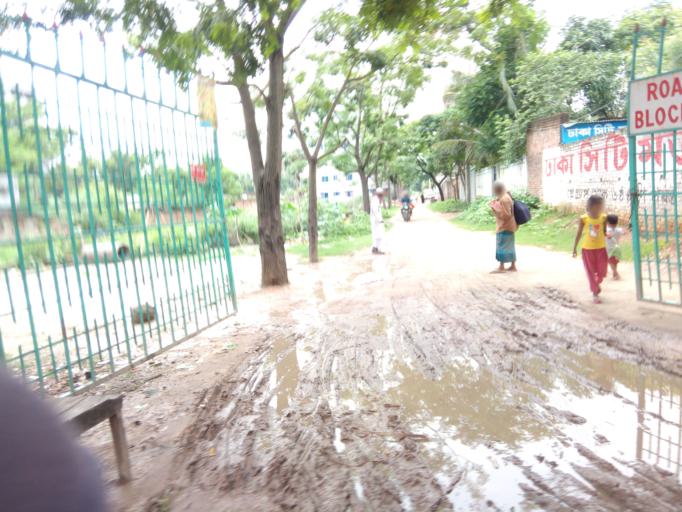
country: BD
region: Dhaka
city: Azimpur
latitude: 23.7612
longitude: 90.3436
